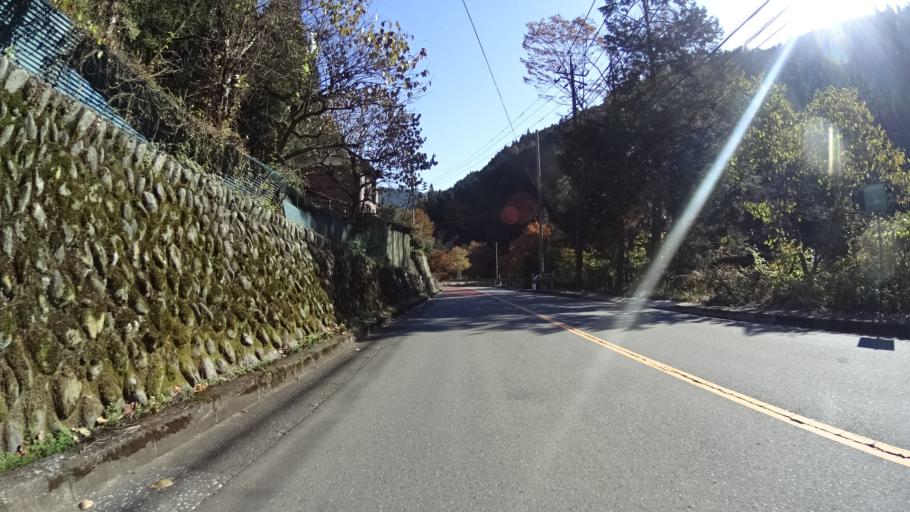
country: JP
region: Yamanashi
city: Uenohara
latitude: 35.7106
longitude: 139.0927
